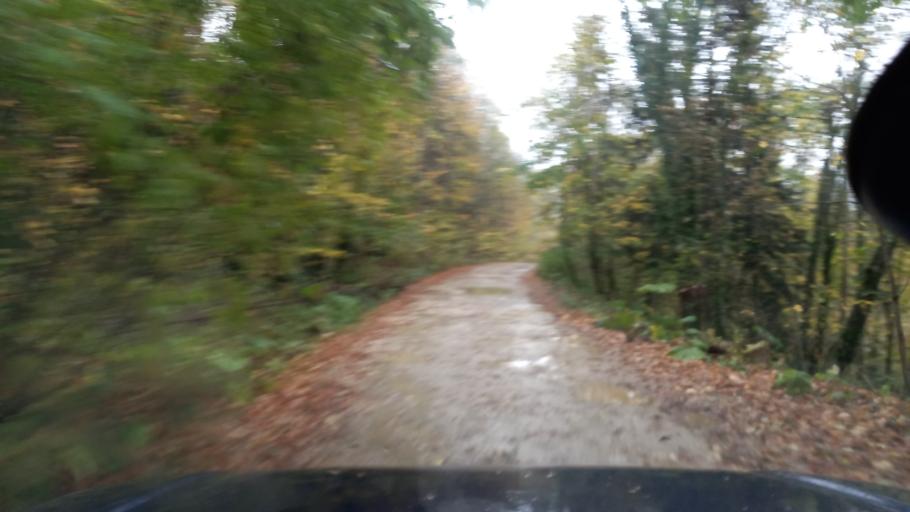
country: RU
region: Krasnodarskiy
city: Neftegorsk
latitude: 44.0404
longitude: 39.8331
